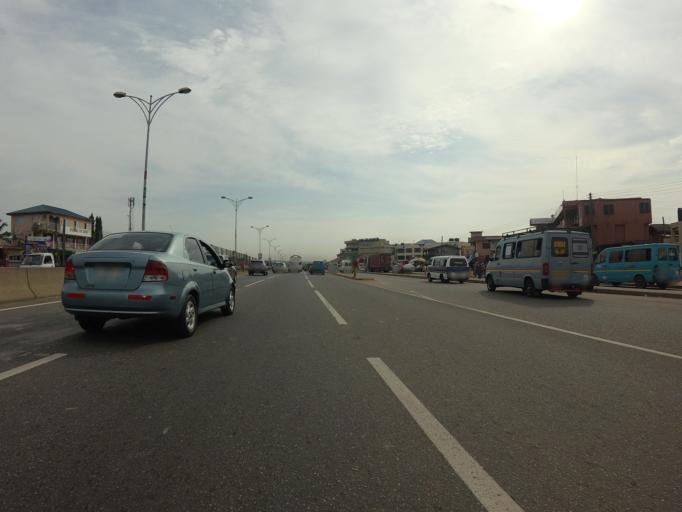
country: GH
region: Greater Accra
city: Dome
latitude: 5.6052
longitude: -0.2521
